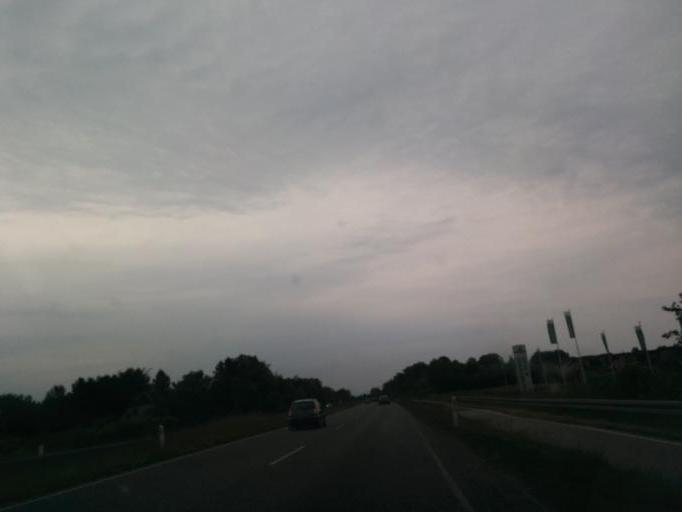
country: DK
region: Central Jutland
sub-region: Arhus Kommune
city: Hjortshoj
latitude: 56.2264
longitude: 10.2912
